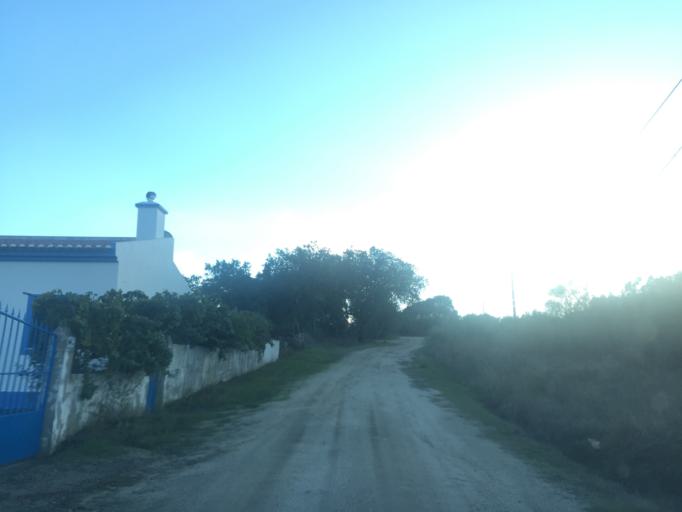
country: PT
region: Portalegre
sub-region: Alter do Chao
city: Alter do Chao
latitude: 39.1868
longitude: -7.6285
